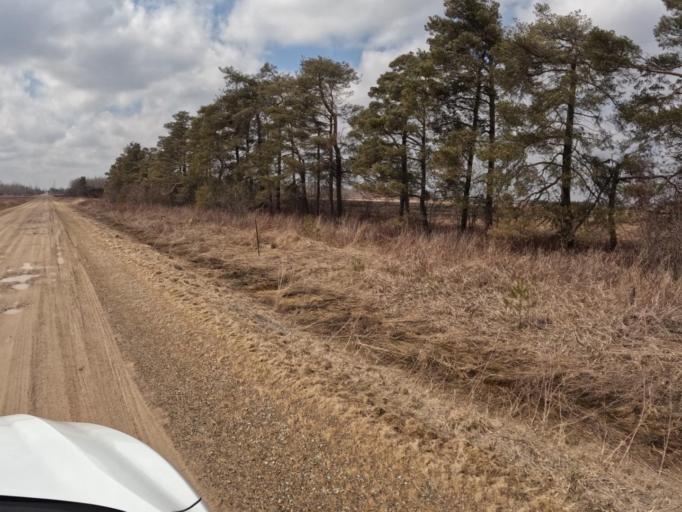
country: CA
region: Ontario
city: Shelburne
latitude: 44.0216
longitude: -80.2919
